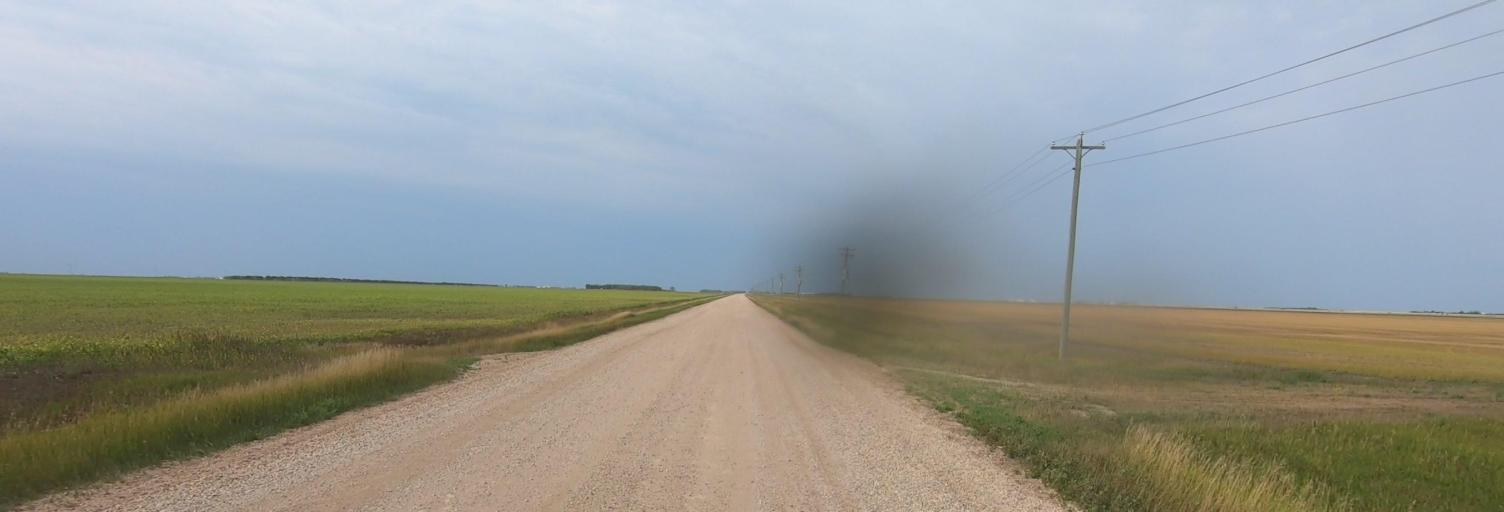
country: CA
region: Manitoba
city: Morris
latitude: 49.5749
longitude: -97.2878
